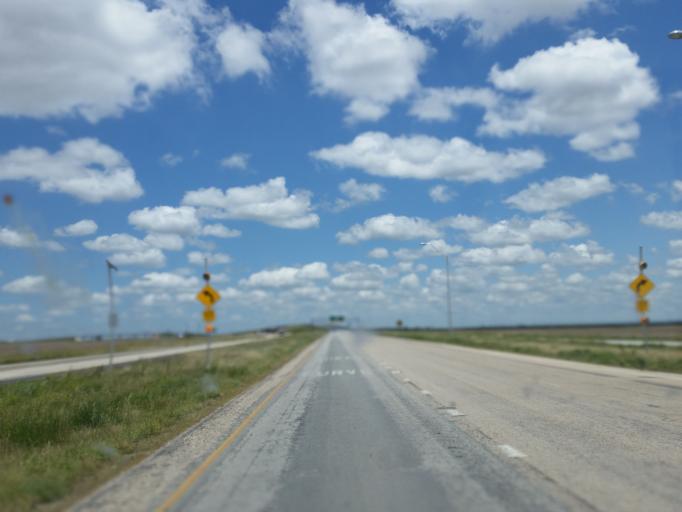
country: US
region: Texas
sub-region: Nolan County
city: Roscoe
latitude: 32.4475
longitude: -100.5142
